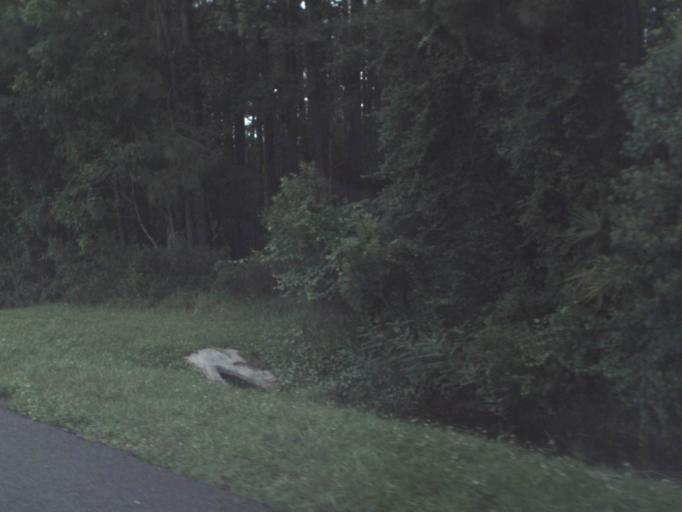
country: US
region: Florida
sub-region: Duval County
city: Baldwin
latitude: 30.2546
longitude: -81.8757
